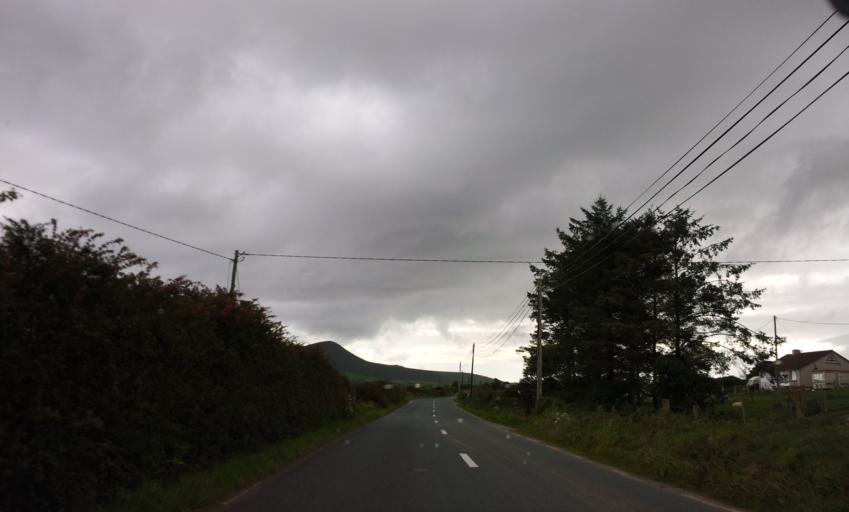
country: IE
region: Munster
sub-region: Ciarrai
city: Killorglin
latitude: 52.1861
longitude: -9.9553
